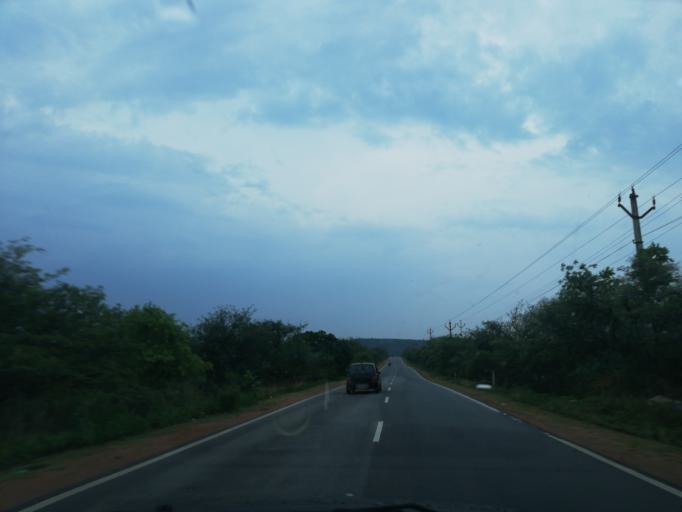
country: IN
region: Andhra Pradesh
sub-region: Guntur
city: Macherla
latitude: 16.6387
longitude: 79.2899
